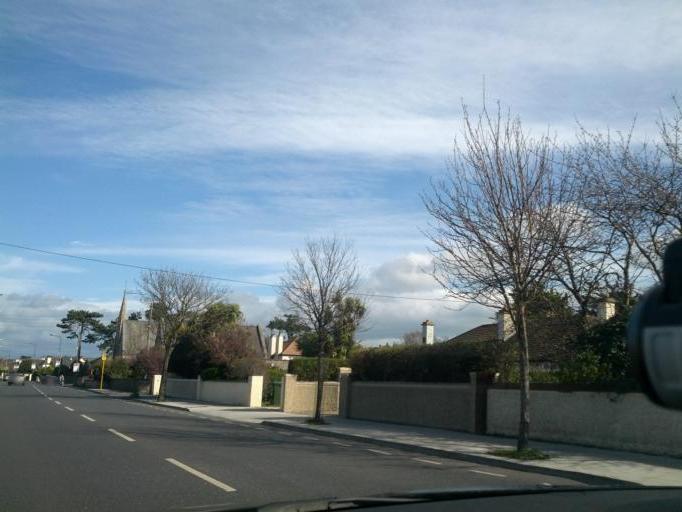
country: IE
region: Leinster
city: Sutton
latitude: 53.3899
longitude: -6.1063
